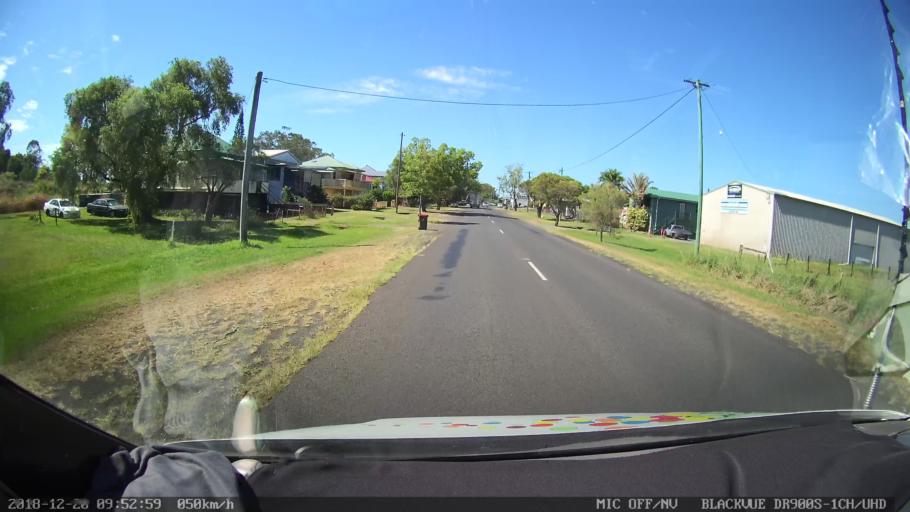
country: AU
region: New South Wales
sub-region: Lismore Municipality
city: Lismore
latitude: -28.7995
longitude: 153.2702
